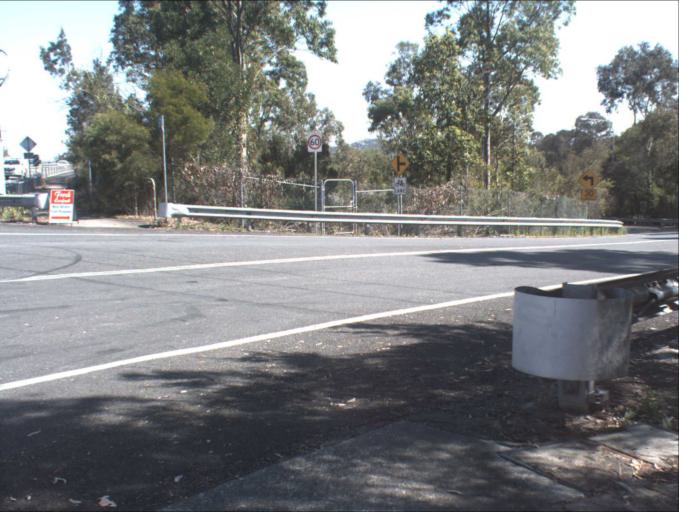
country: AU
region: Queensland
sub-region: Logan
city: Beenleigh
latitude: -27.6987
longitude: 153.1968
